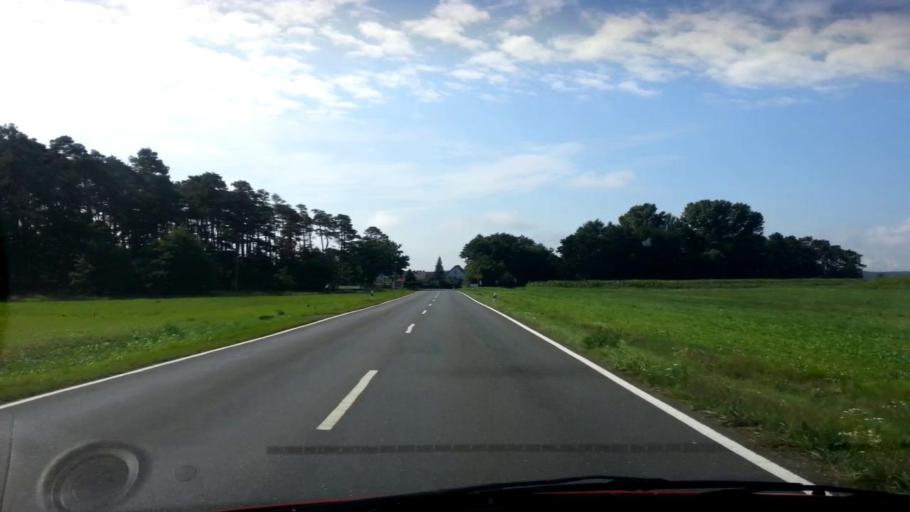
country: DE
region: Bavaria
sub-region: Upper Franconia
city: Hausen
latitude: 49.6930
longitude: 11.0377
